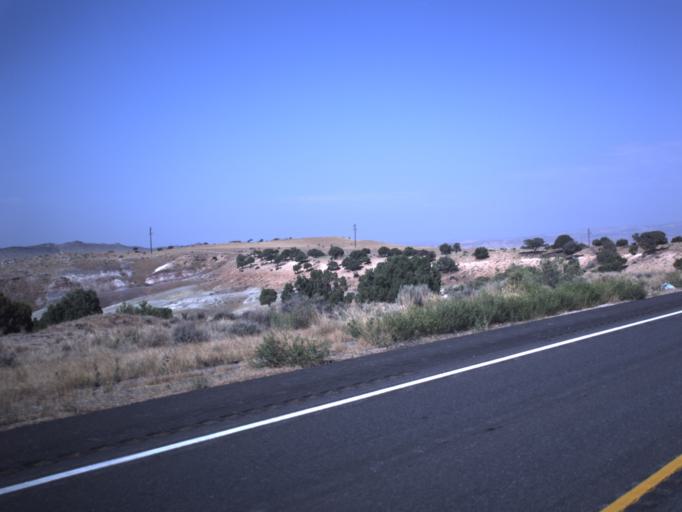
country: US
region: Utah
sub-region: Uintah County
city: Naples
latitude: 40.3227
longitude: -109.2616
